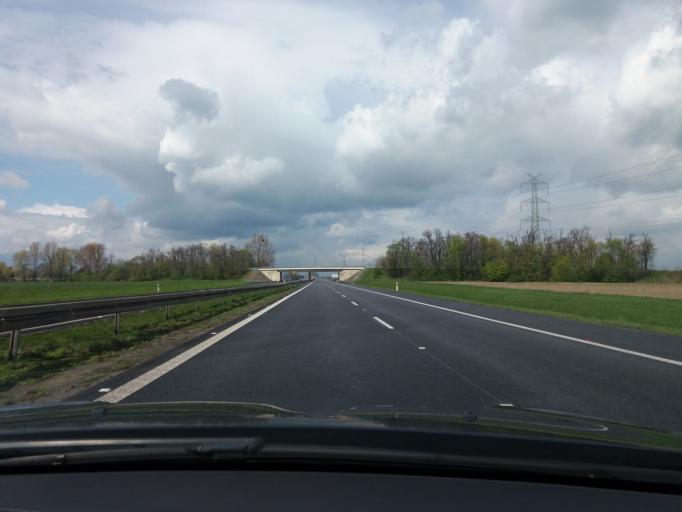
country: PL
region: Lower Silesian Voivodeship
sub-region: Powiat olawski
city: Wierzbno
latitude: 50.8870
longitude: 17.1919
